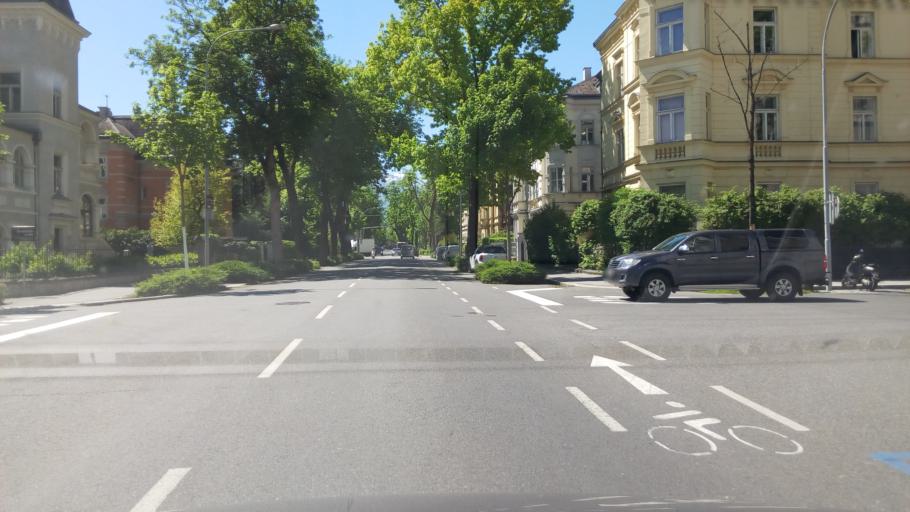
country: AT
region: Tyrol
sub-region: Innsbruck Stadt
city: Innsbruck
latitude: 47.2752
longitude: 11.4008
